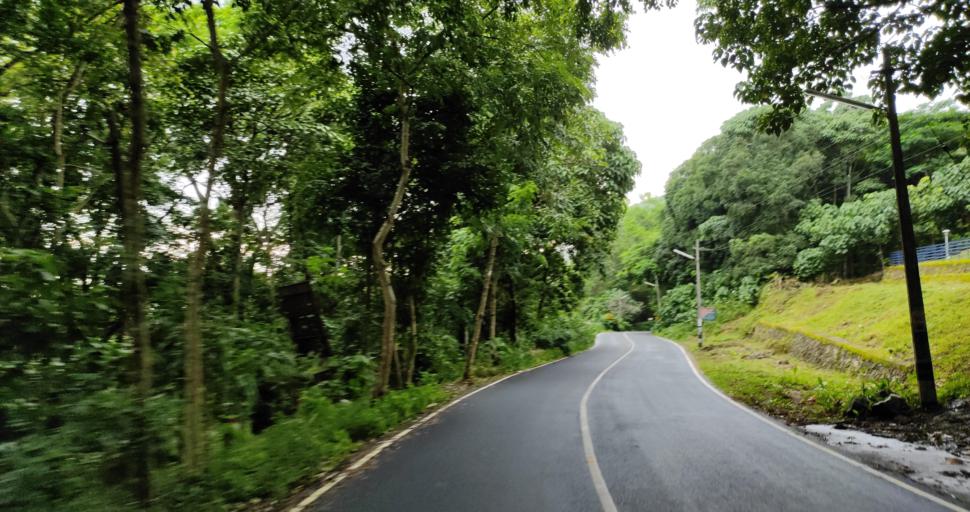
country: IN
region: Kerala
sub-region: Ernakulam
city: Angamali
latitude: 10.2988
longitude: 76.4544
